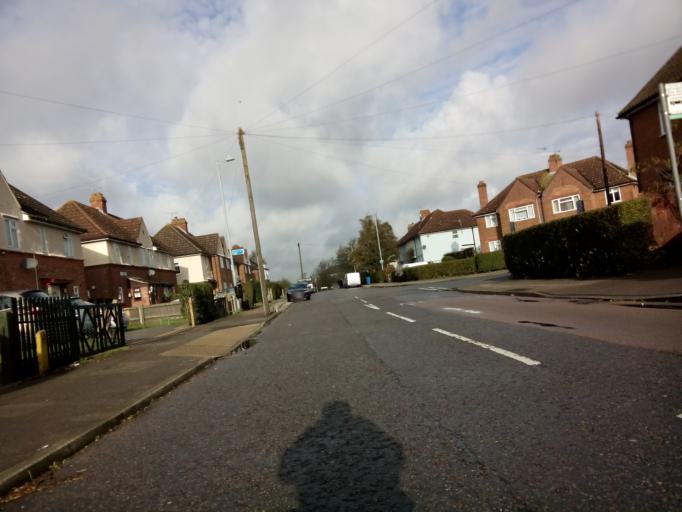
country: GB
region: England
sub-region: Suffolk
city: Bramford
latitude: 52.0845
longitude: 1.1270
